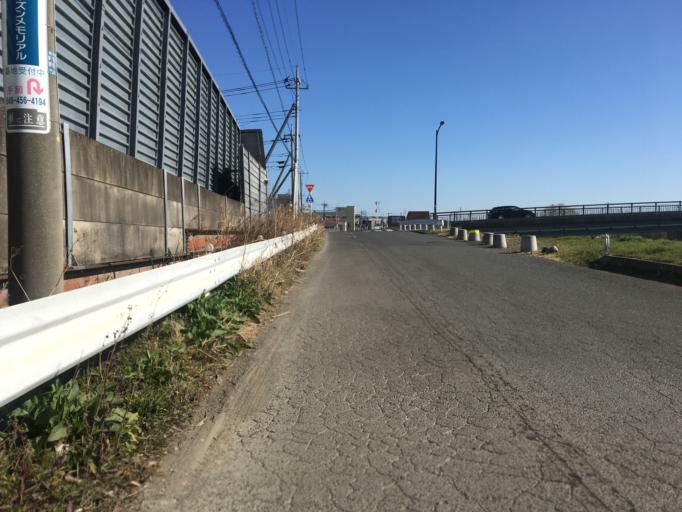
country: JP
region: Saitama
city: Asaka
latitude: 35.8209
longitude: 139.6073
